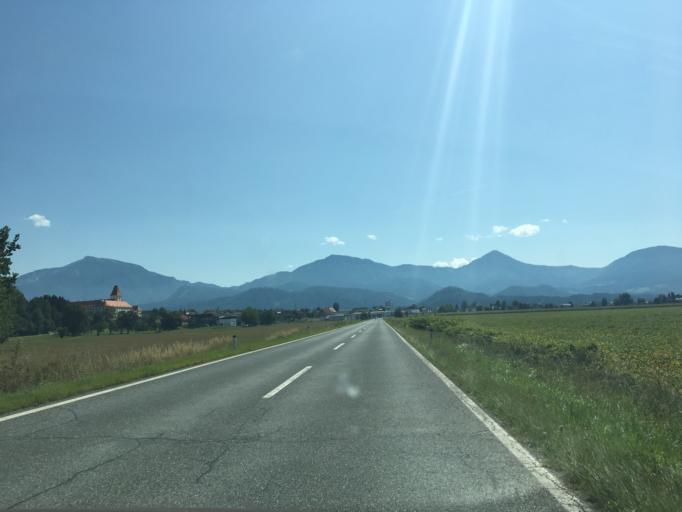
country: AT
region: Carinthia
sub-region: Politischer Bezirk Volkermarkt
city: Eberndorf
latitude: 46.5976
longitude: 14.6342
